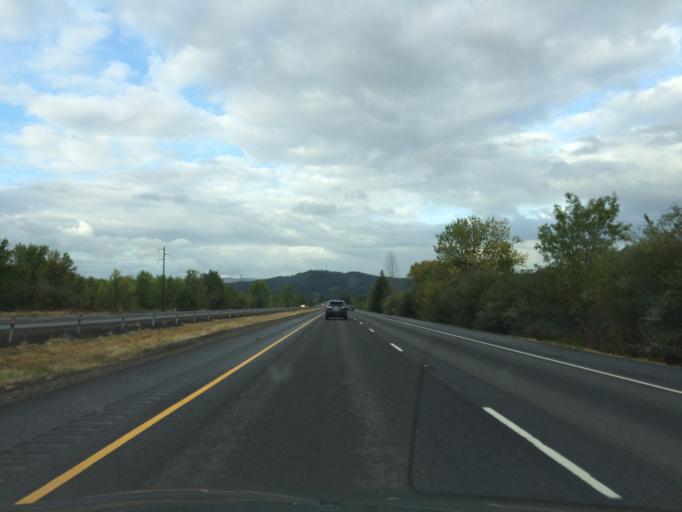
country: US
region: Oregon
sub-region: Lane County
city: Cottage Grove
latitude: 43.7589
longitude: -123.0896
